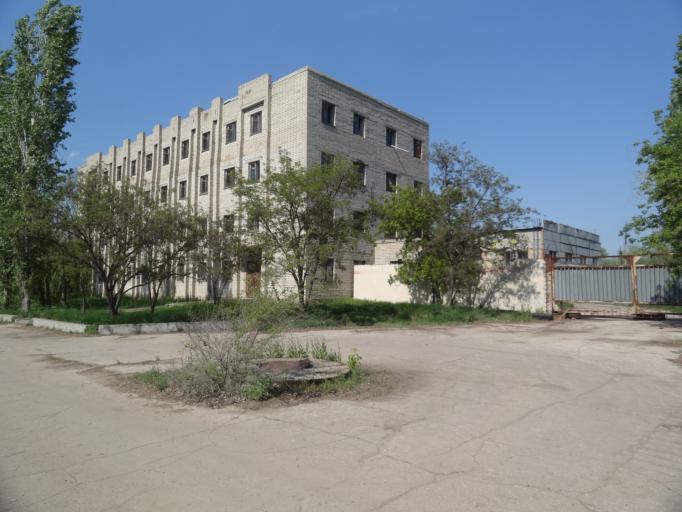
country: RU
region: Saratov
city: Privolzhskiy
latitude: 51.3932
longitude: 46.0802
